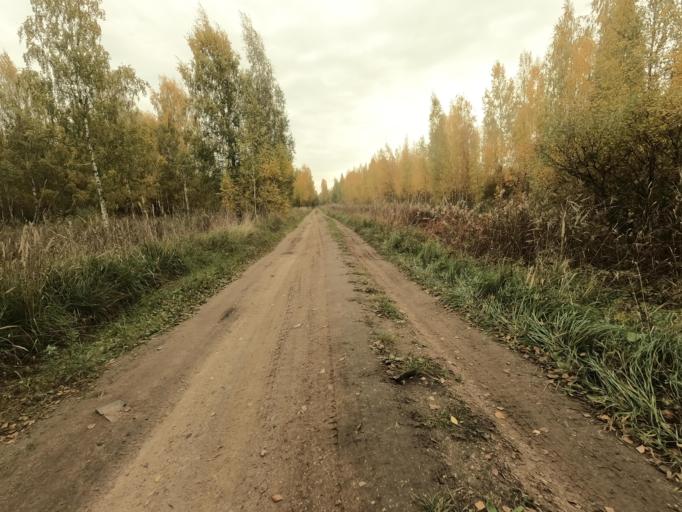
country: RU
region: Novgorod
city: Pankovka
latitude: 58.8661
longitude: 30.9253
